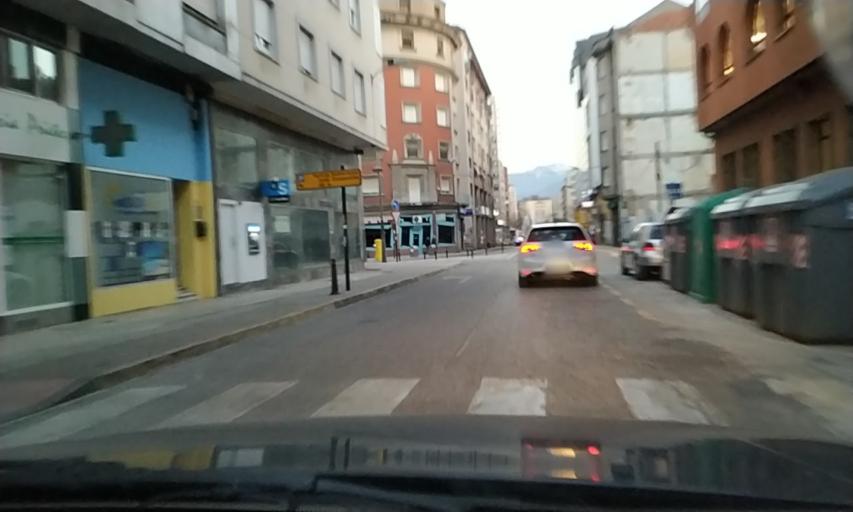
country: ES
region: Castille and Leon
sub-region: Provincia de Leon
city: Ponferrada
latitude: 42.5493
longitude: -6.5987
